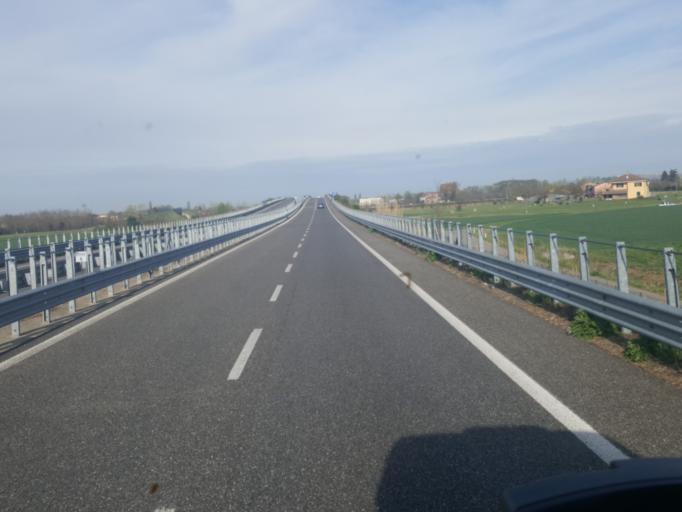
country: IT
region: Piedmont
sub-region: Provincia di Alessandria
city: Alessandria
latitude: 44.9338
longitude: 8.5982
